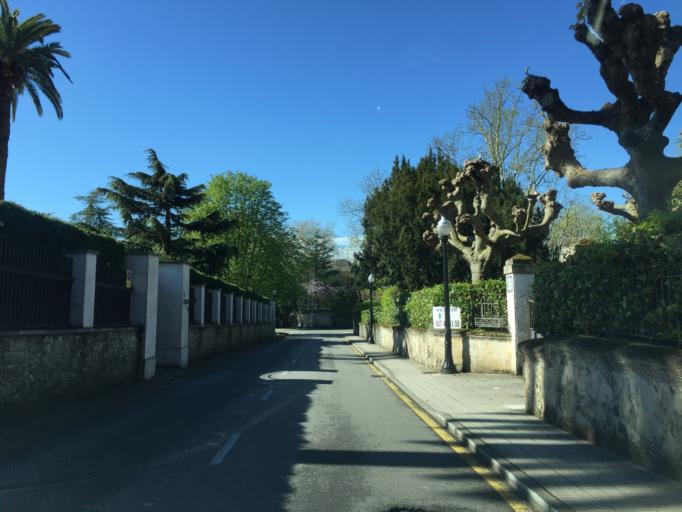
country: ES
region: Asturias
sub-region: Province of Asturias
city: Gijon
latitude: 43.5347
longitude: -5.6237
